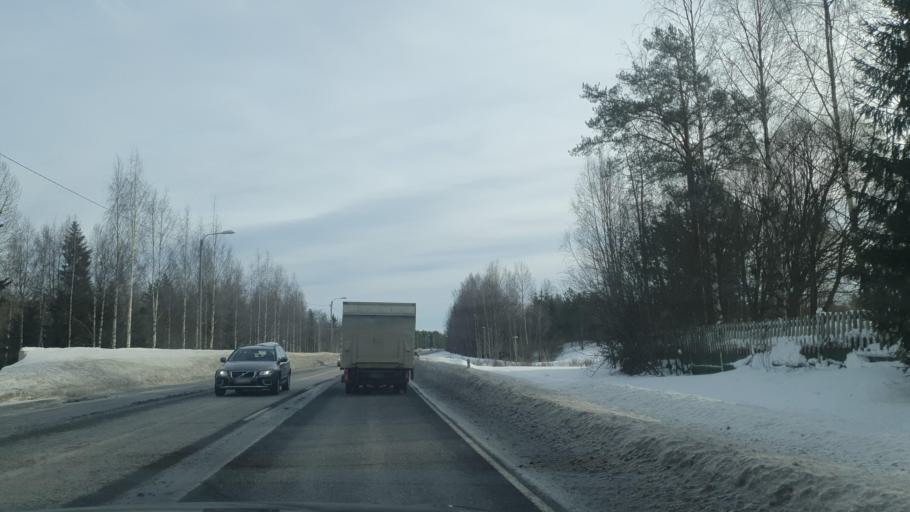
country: FI
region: Northern Ostrobothnia
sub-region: Oulu
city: Kempele
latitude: 64.9676
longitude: 25.6271
